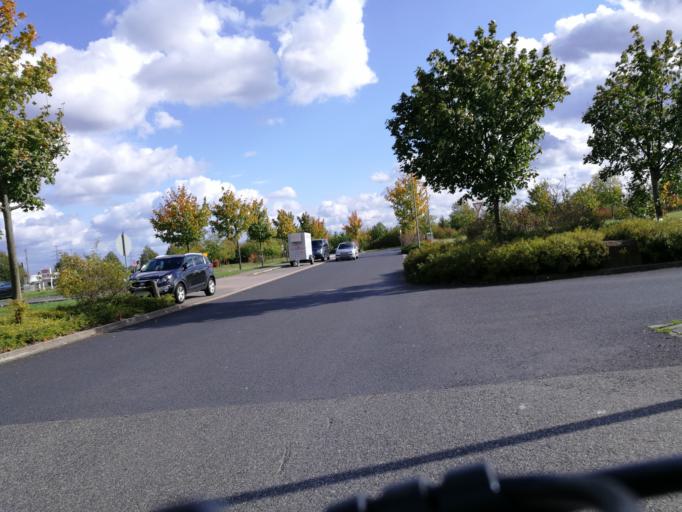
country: DE
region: North Rhine-Westphalia
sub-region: Regierungsbezirk Dusseldorf
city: Dusseldorf
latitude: 51.1454
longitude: 6.7558
